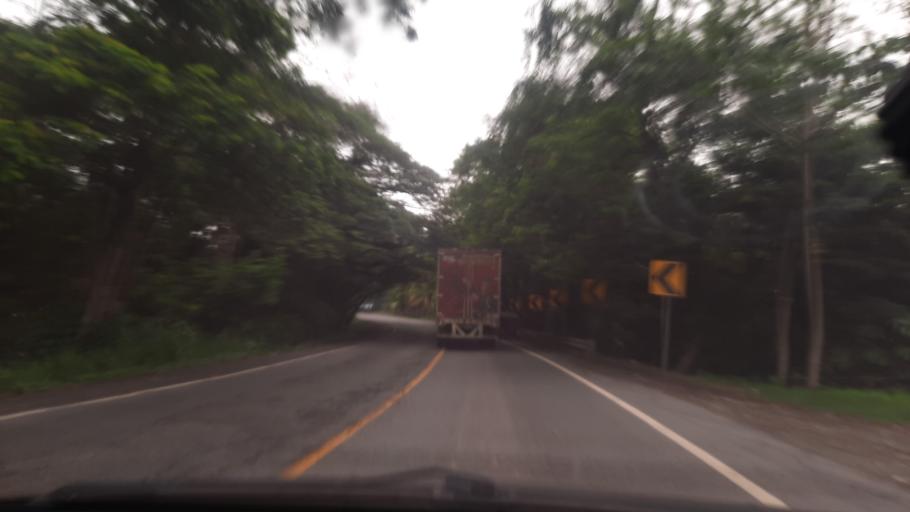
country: GT
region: Izabal
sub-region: Municipio de Los Amates
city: Los Amates
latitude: 15.2774
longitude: -89.0751
